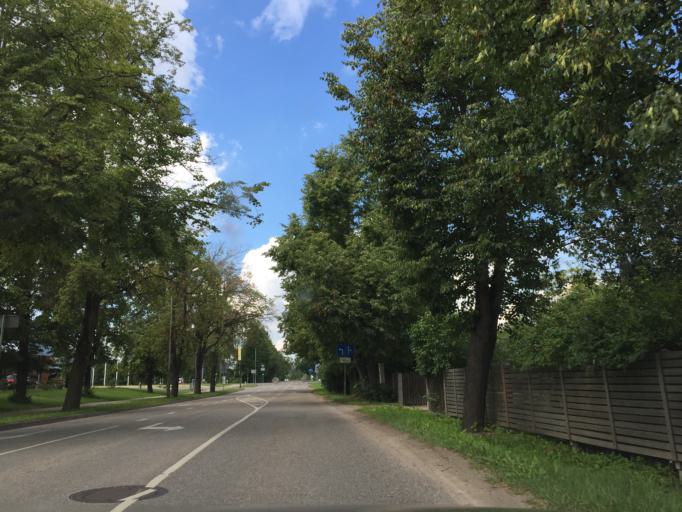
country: LV
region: Jelgava
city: Jelgava
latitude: 56.6572
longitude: 23.7448
